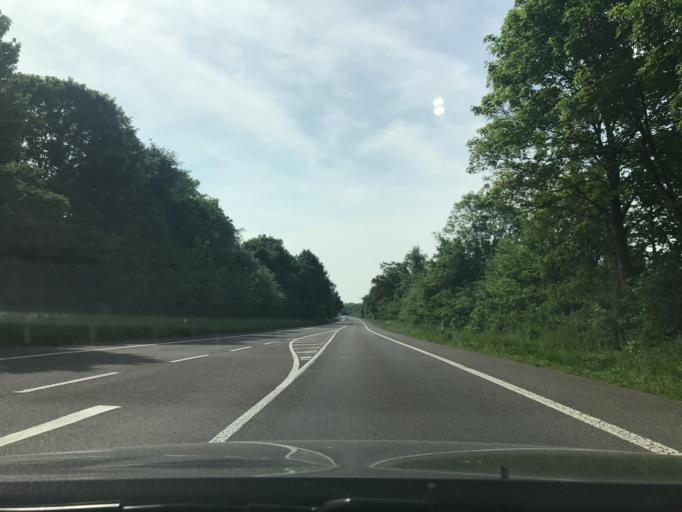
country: DE
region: North Rhine-Westphalia
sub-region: Regierungsbezirk Dusseldorf
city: Wachtendonk
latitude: 51.3963
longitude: 6.3002
